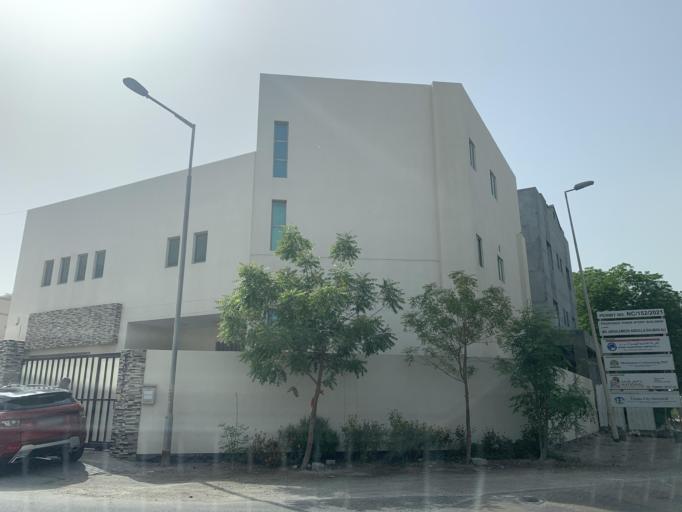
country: BH
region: Northern
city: Ar Rifa'
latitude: 26.1302
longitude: 50.5917
